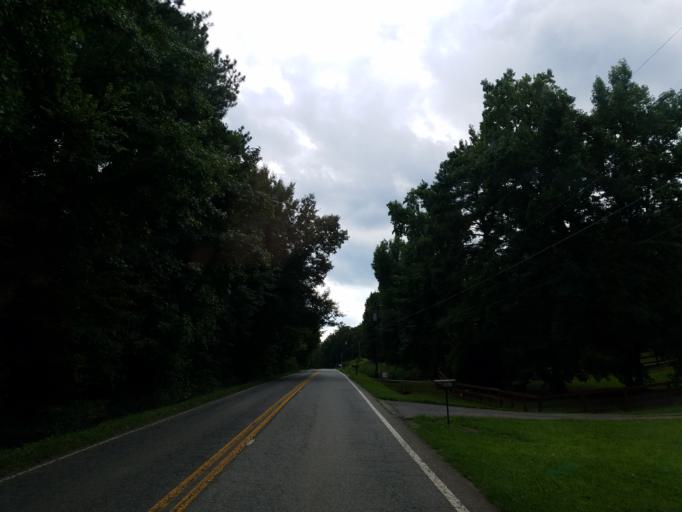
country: US
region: Georgia
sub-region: Bartow County
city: Cartersville
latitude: 34.2648
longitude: -84.8342
